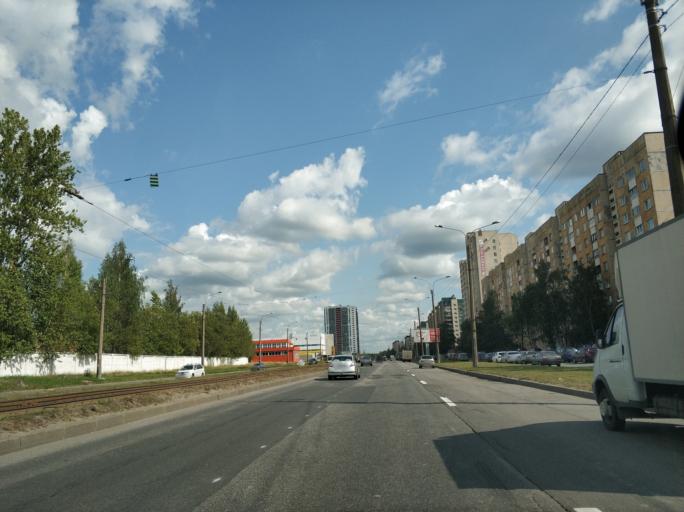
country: RU
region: St.-Petersburg
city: Krasnogvargeisky
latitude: 59.9565
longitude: 30.4693
